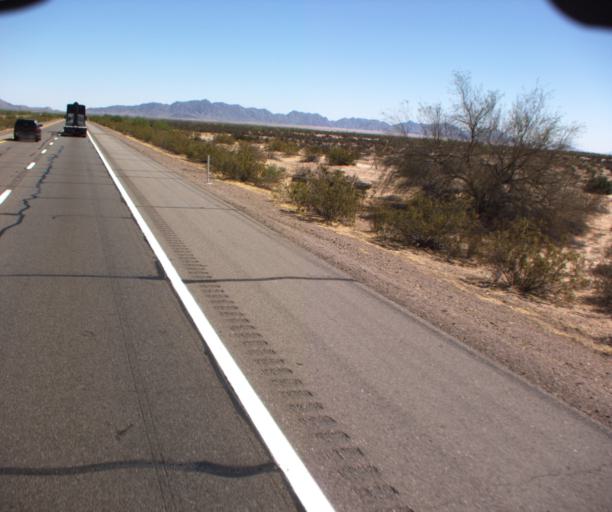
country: US
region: Arizona
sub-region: Yuma County
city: Wellton
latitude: 32.7012
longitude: -113.9019
